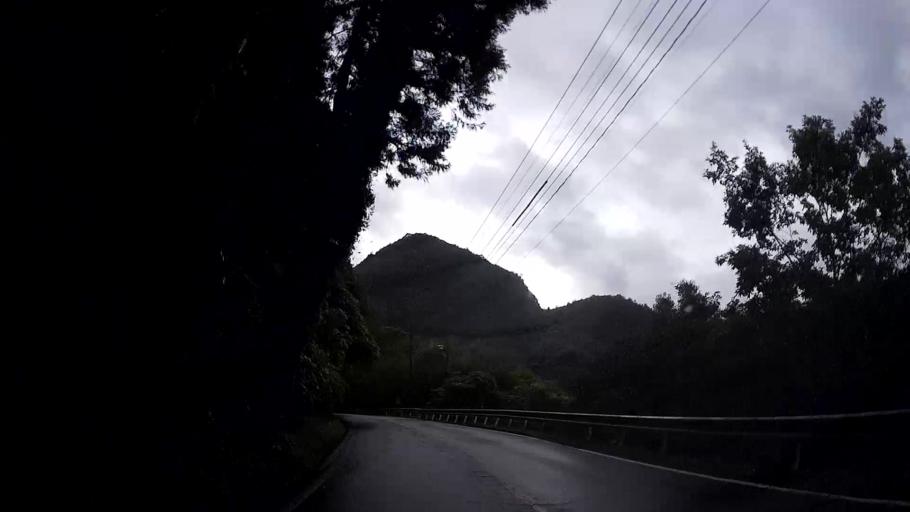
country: JP
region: Oita
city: Hita
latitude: 33.1795
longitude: 131.0060
